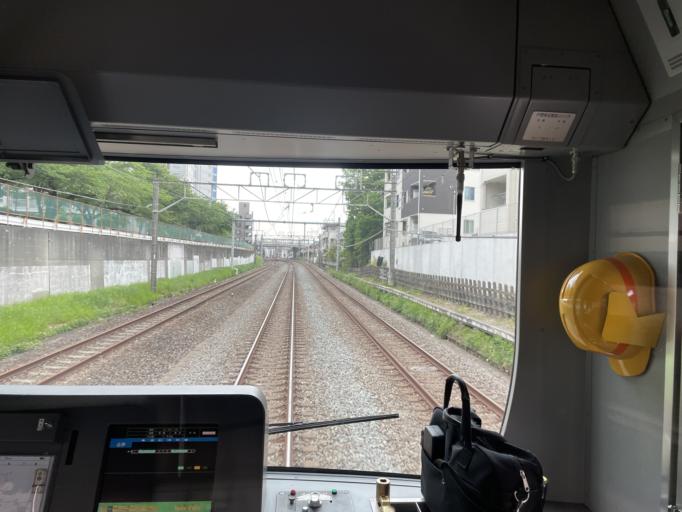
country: JP
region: Saitama
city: Tokorozawa
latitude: 35.7877
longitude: 139.4833
